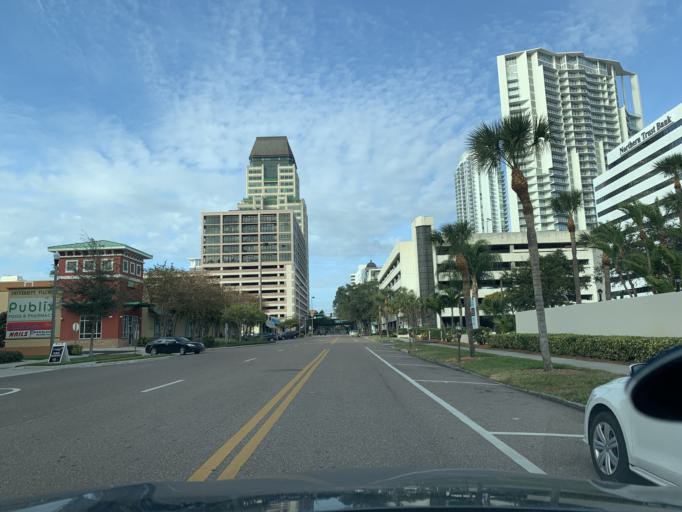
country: US
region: Florida
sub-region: Pinellas County
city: Saint Petersburg
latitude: 27.7678
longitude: -82.6355
